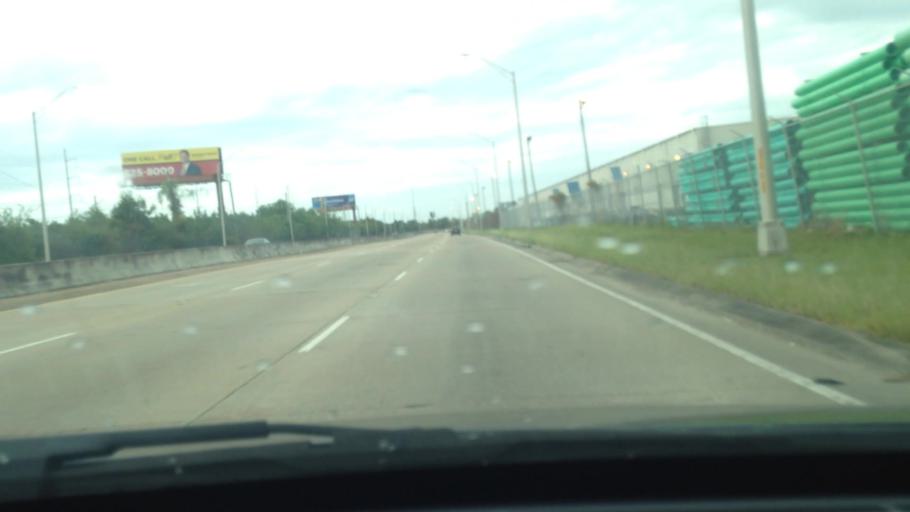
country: US
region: Louisiana
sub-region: Jefferson Parish
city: Jefferson
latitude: 29.9701
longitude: -90.1457
